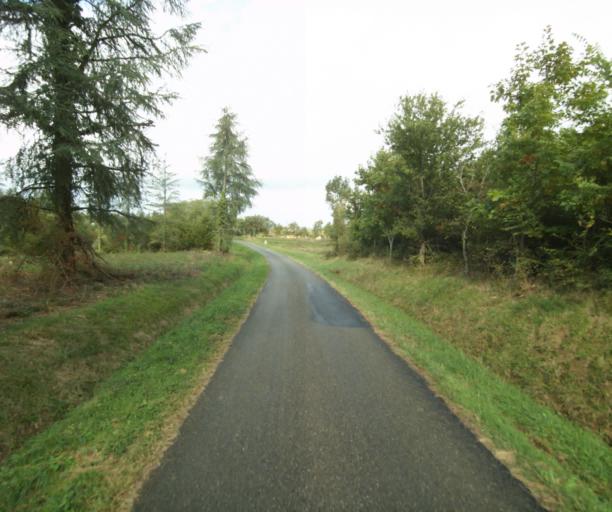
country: FR
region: Midi-Pyrenees
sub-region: Departement du Gers
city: Cazaubon
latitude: 43.8594
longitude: -0.0395
